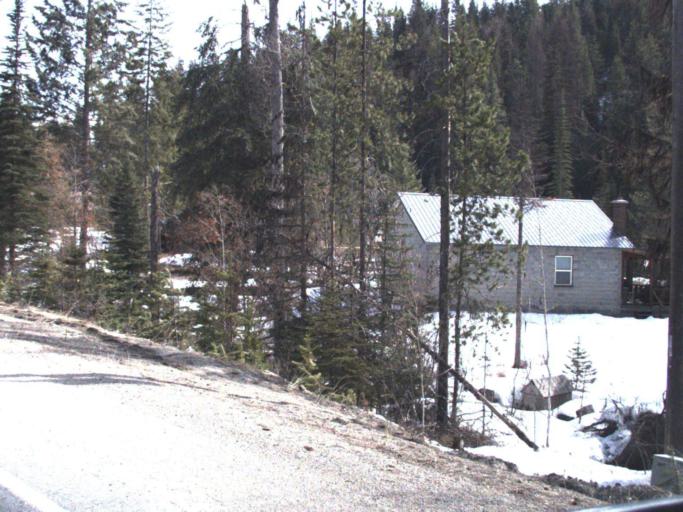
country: US
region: Washington
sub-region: Stevens County
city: Chewelah
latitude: 48.5367
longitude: -117.6059
